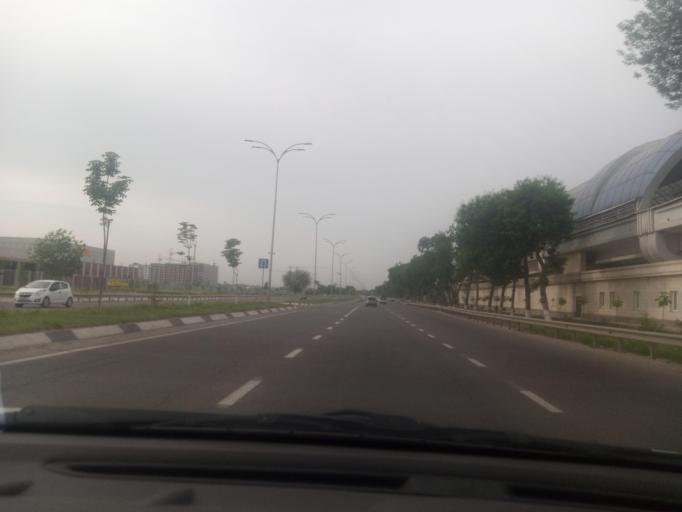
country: UZ
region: Toshkent Shahri
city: Bektemir
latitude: 41.2827
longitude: 69.3606
